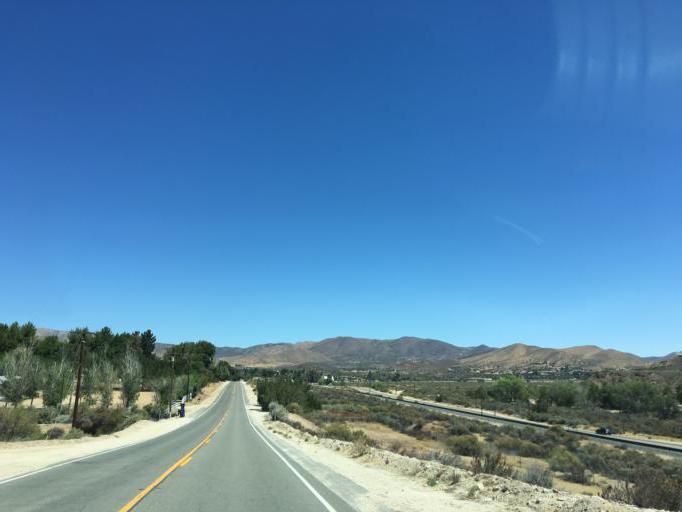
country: US
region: California
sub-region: Los Angeles County
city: Acton
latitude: 34.4600
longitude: -118.1980
